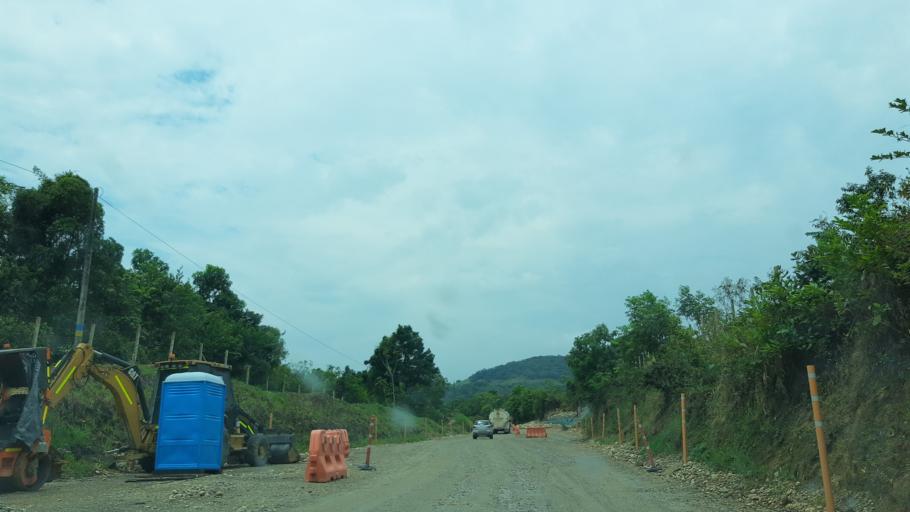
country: CO
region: Casanare
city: Sabanalarga
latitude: 4.7752
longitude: -73.0025
